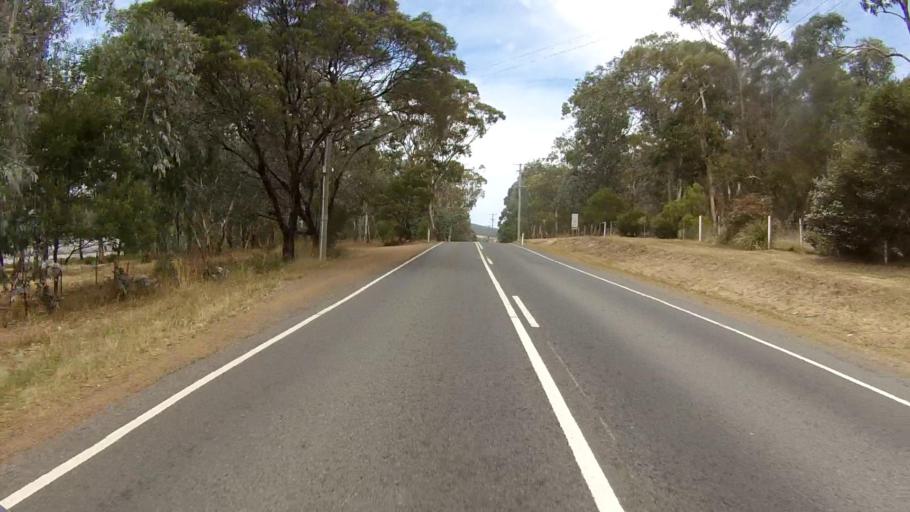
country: AU
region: Tasmania
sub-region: Clarence
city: Lauderdale
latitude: -42.8973
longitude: 147.4806
